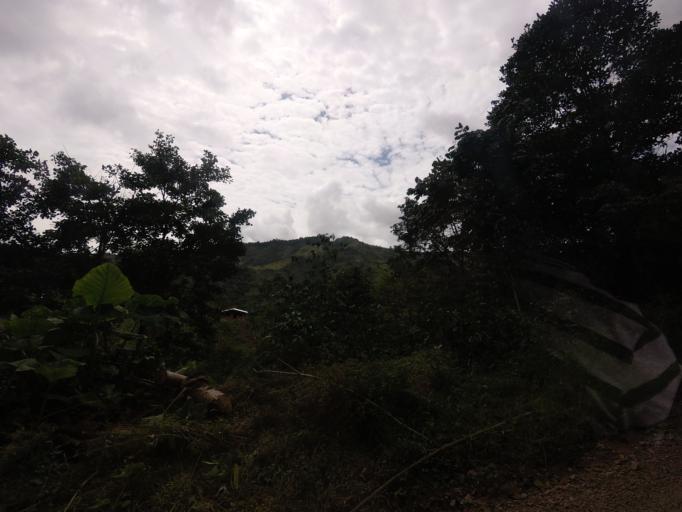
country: CO
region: Huila
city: San Agustin
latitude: 1.9297
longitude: -76.2998
